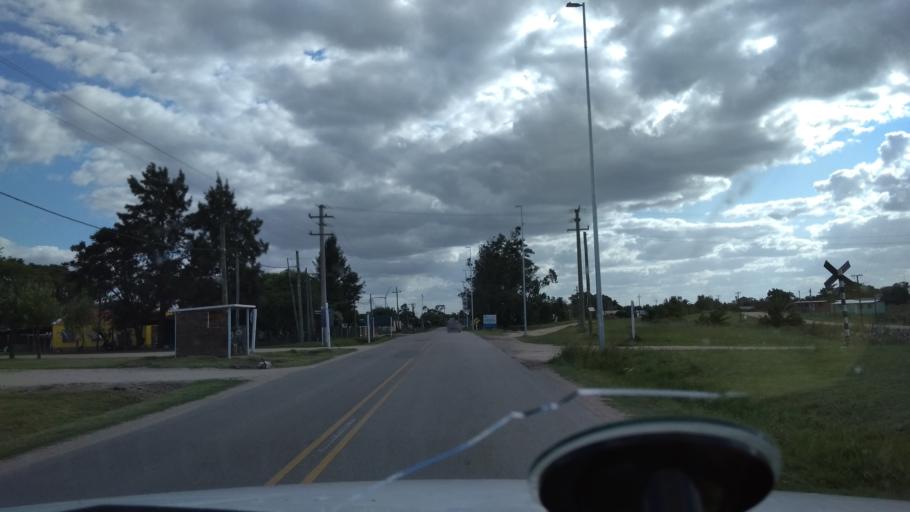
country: UY
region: Canelones
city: Tala
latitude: -34.1928
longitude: -55.7290
